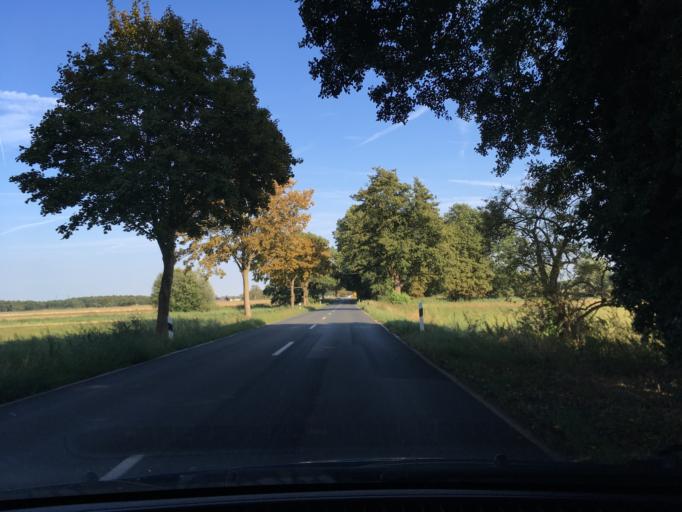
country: DE
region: Lower Saxony
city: Isernhagen Farster Bauerschaft
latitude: 52.4883
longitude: 9.8665
